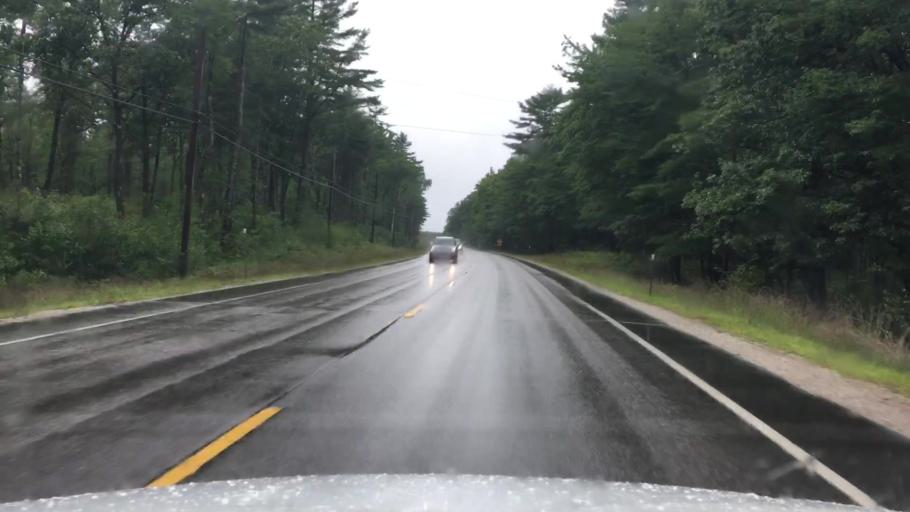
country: US
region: Maine
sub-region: Oxford County
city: Fryeburg
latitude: 43.9990
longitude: -71.0111
